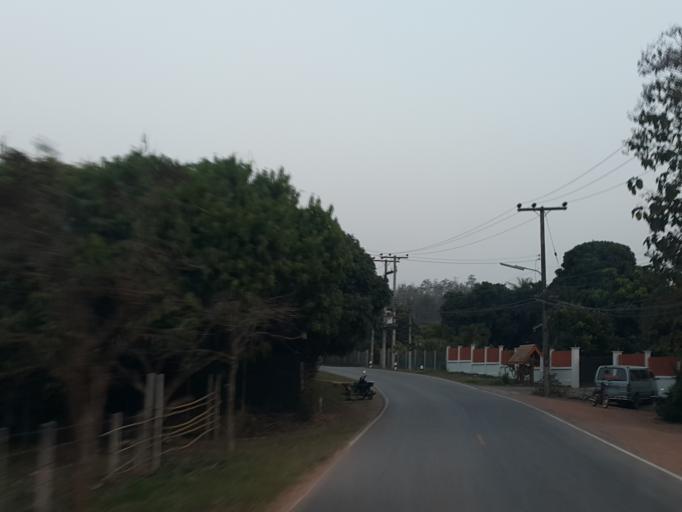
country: TH
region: Chiang Mai
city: Mae Taeng
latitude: 18.9872
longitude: 98.9050
